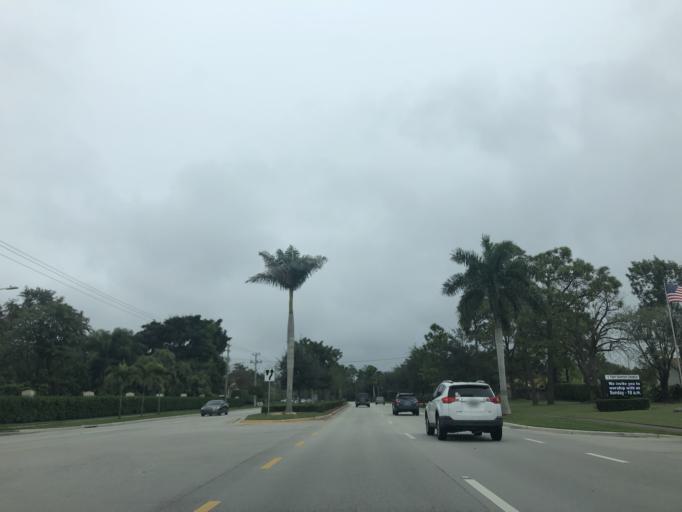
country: US
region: Florida
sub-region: Palm Beach County
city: Wellington
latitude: 26.6674
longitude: -80.2457
